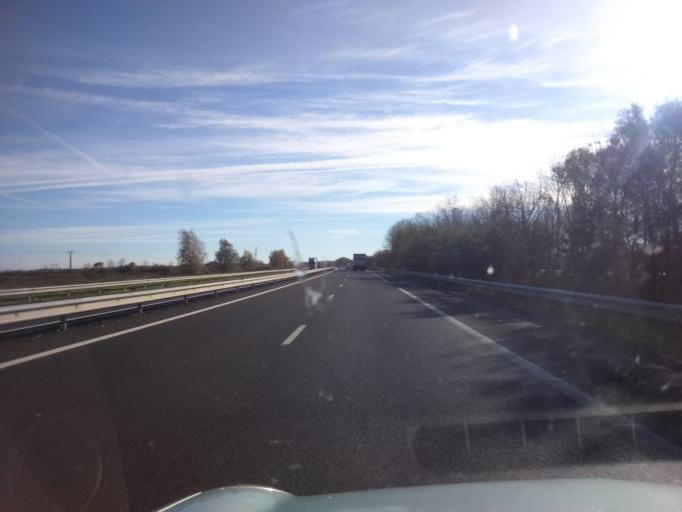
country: FR
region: Poitou-Charentes
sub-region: Departement de la Charente-Maritime
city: Breuil-Magne
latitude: 45.9585
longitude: -0.9421
